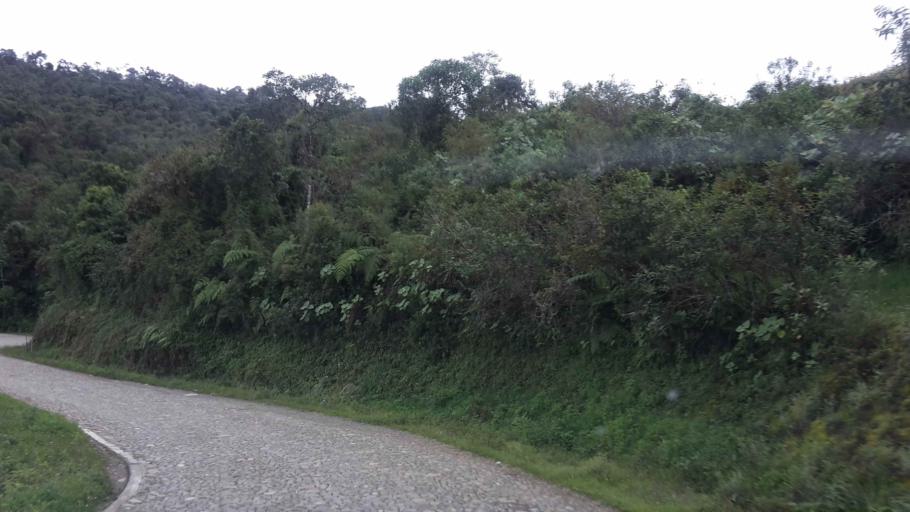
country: BO
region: Cochabamba
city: Colomi
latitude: -17.1593
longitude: -65.9066
